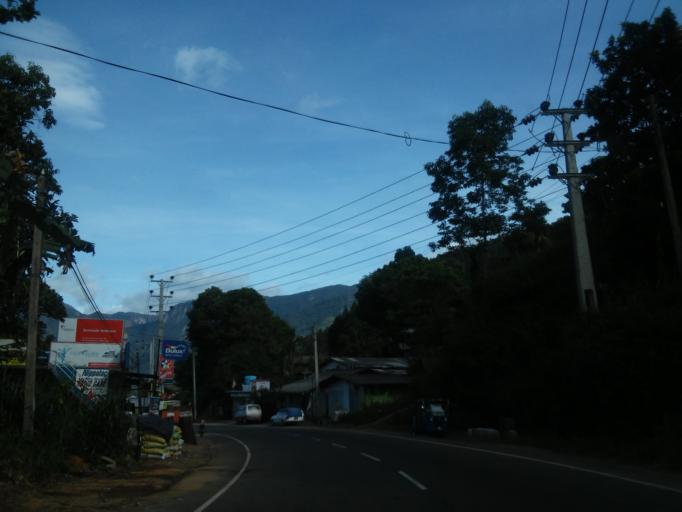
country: LK
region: Uva
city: Haputale
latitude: 6.7609
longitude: 80.8798
